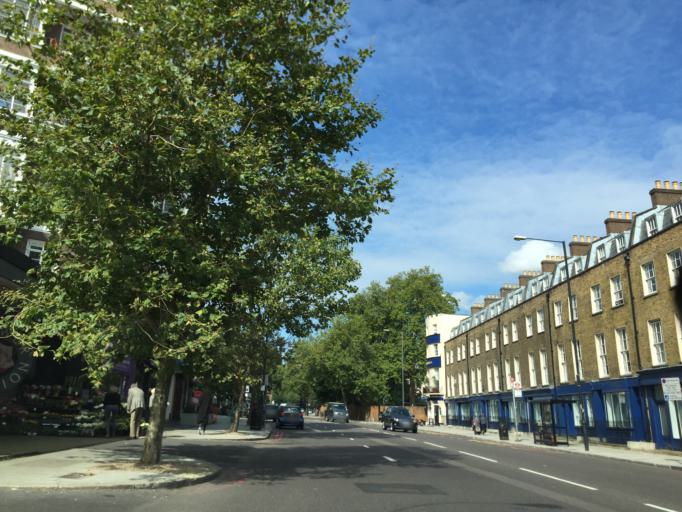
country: GB
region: England
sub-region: Greater London
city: Camden Town
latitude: 51.5257
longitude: -0.1615
